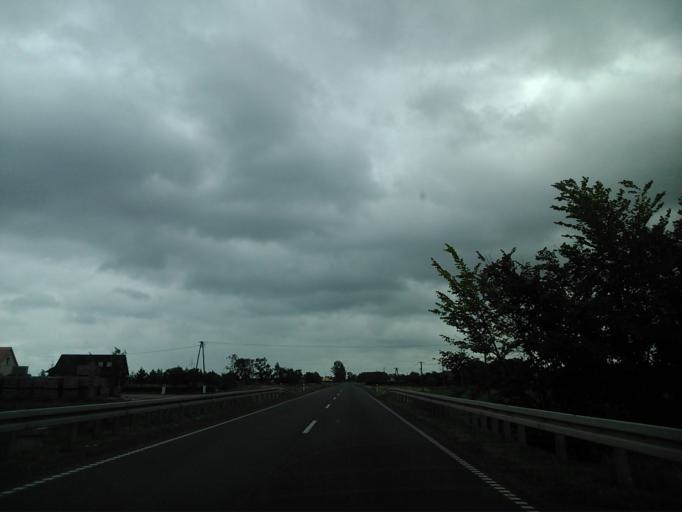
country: PL
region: Kujawsko-Pomorskie
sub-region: Powiat inowroclawski
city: Kruszwica
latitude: 52.6631
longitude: 18.3562
